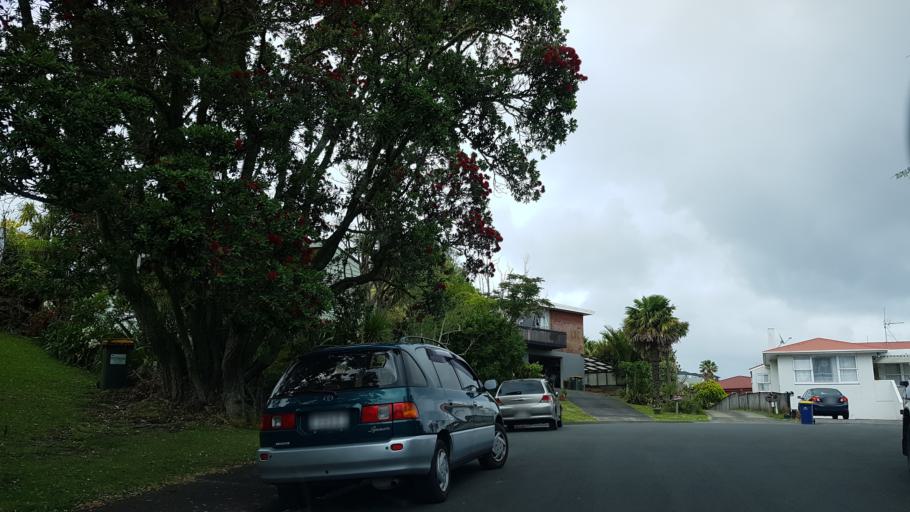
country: NZ
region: Auckland
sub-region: Auckland
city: North Shore
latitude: -36.7877
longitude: 174.7371
